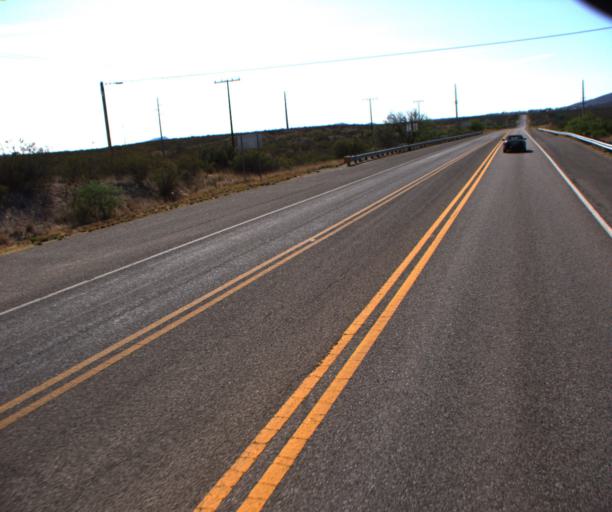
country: US
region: Arizona
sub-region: Cochise County
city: Tombstone
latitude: 31.7474
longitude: -110.0960
